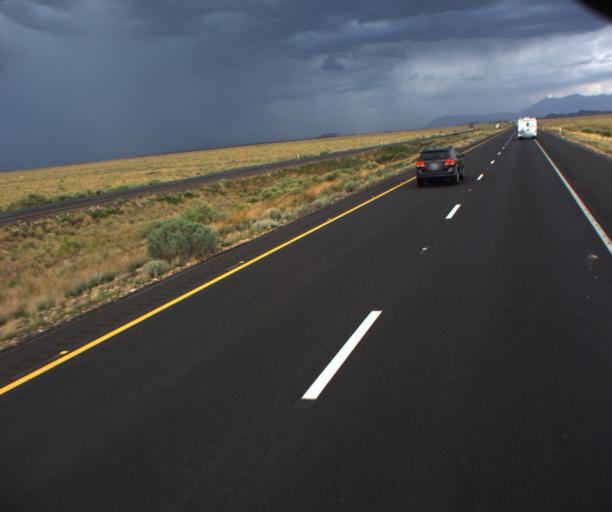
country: US
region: Arizona
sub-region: Coconino County
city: Flagstaff
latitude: 35.1451
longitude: -111.2268
